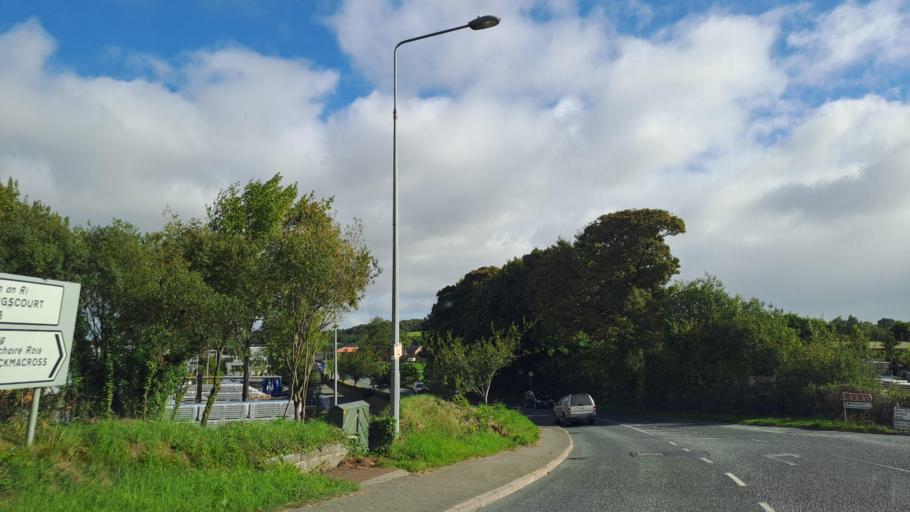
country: IE
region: Ulster
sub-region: An Cabhan
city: Kingscourt
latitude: 53.9037
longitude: -6.7918
